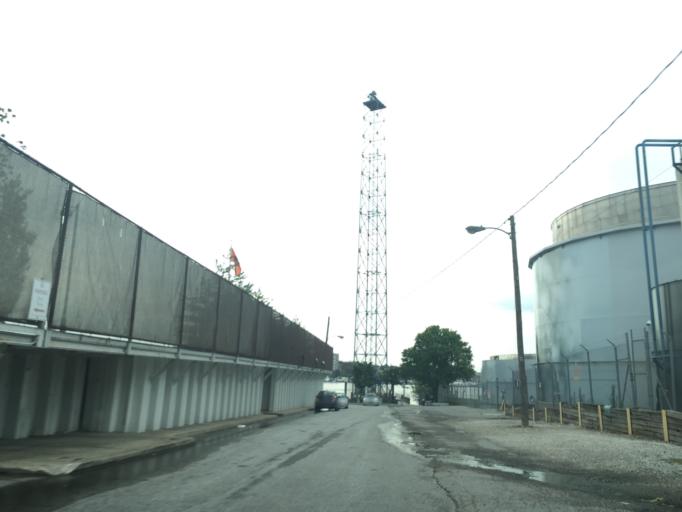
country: US
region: Maryland
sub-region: City of Baltimore
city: Baltimore
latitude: 39.2748
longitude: -76.5904
